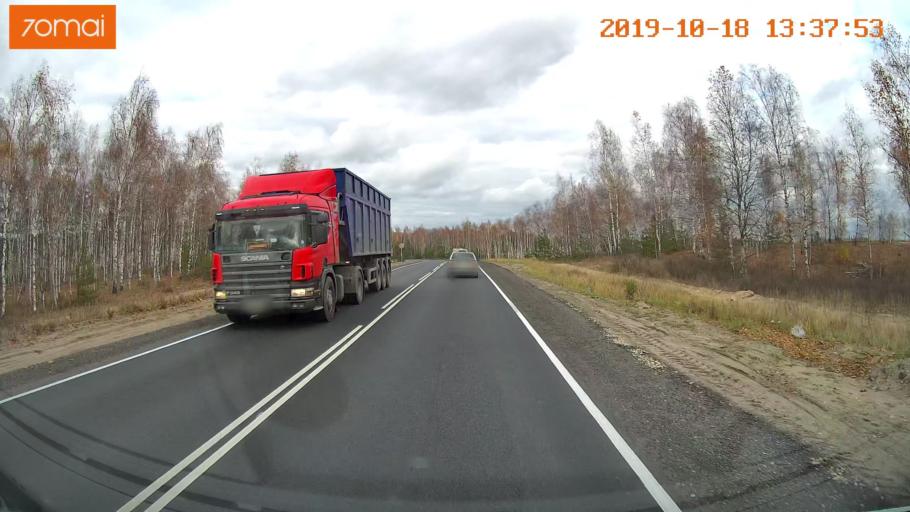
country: RU
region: Rjazan
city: Solotcha
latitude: 54.8838
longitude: 39.9996
